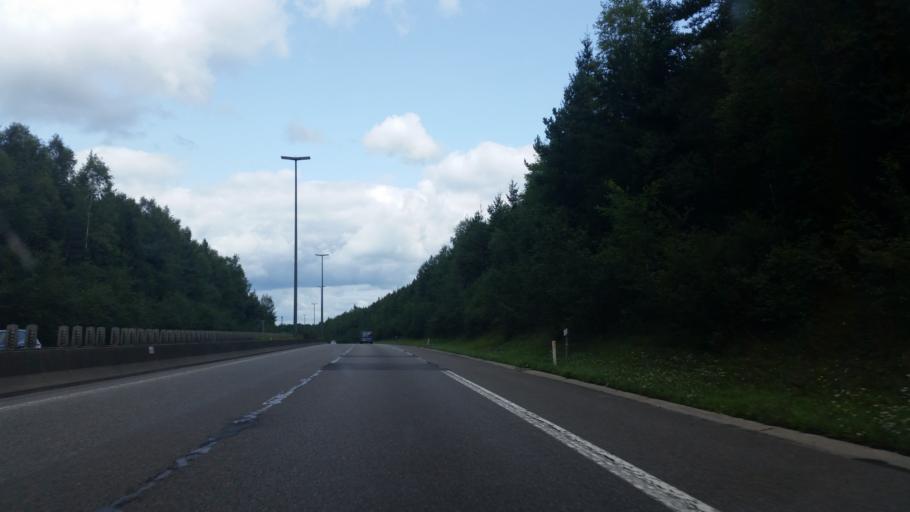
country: BE
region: Wallonia
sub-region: Province du Luxembourg
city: Tellin
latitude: 50.0445
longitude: 5.2124
